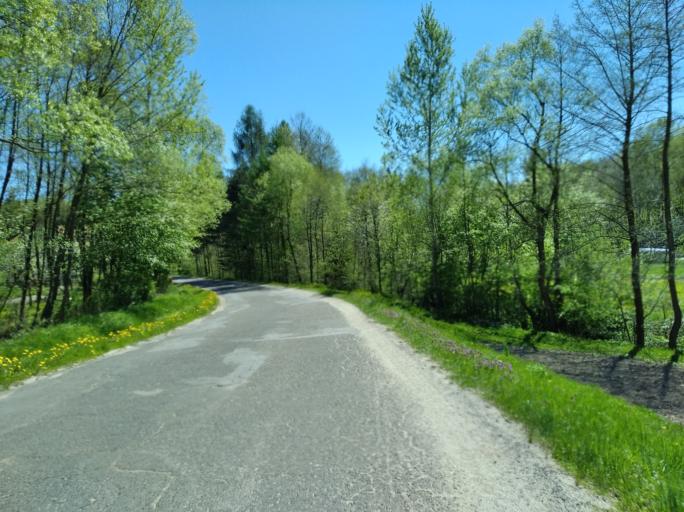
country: PL
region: Subcarpathian Voivodeship
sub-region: Powiat debicki
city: Brzostek
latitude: 49.9081
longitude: 21.4806
